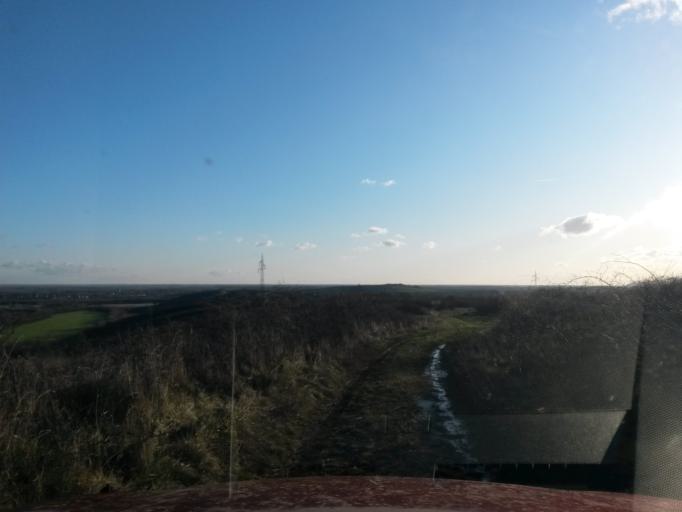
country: HU
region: Borsod-Abauj-Zemplen
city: Sarospatak
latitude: 48.3269
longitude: 21.5382
